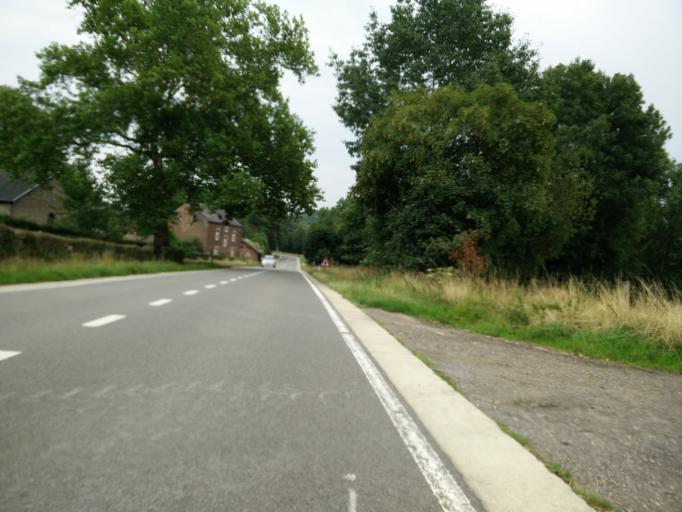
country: BE
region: Wallonia
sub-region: Province de Liege
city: Dalhem
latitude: 50.7136
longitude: 5.7608
